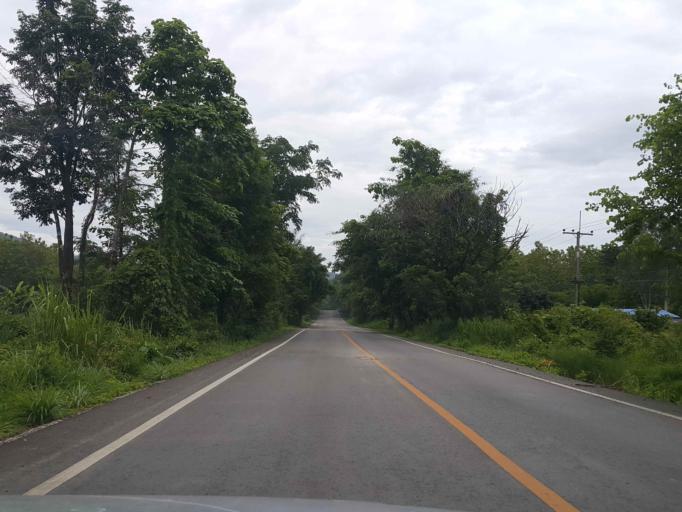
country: TH
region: Lampang
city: Thoen
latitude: 17.5609
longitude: 99.3330
